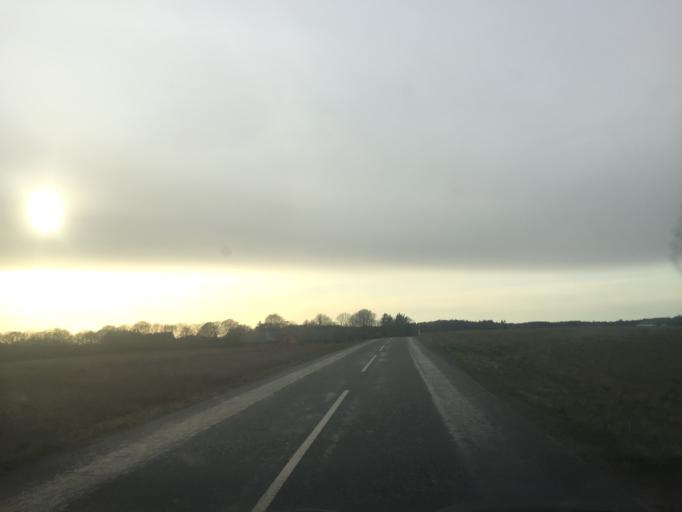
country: DK
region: Zealand
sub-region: Ringsted Kommune
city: Ringsted
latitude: 55.4841
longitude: 11.8294
